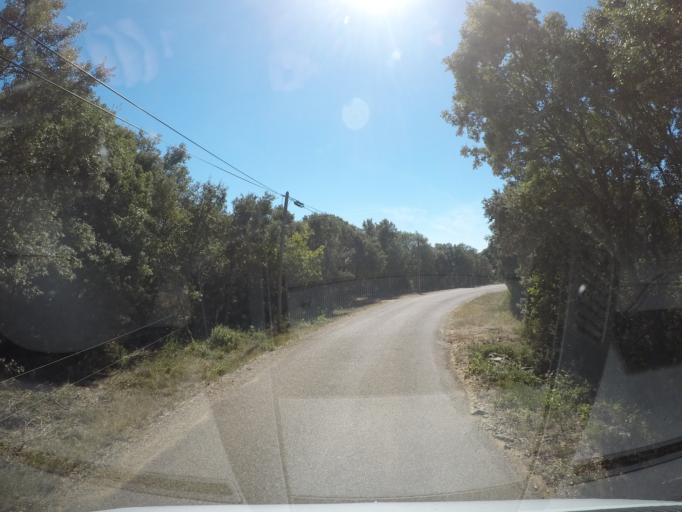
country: FR
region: Languedoc-Roussillon
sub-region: Departement de l'Herault
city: Aniane
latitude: 43.7314
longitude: 3.6507
